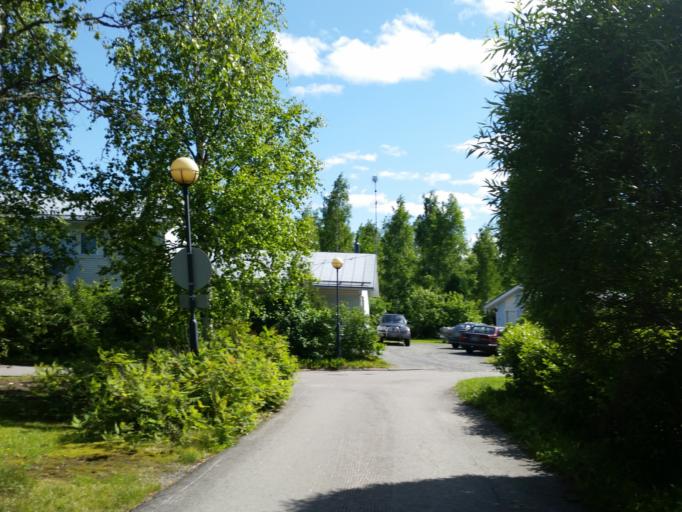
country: FI
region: Northern Savo
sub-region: Varkaus
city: Varkaus
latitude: 62.3360
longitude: 27.9041
